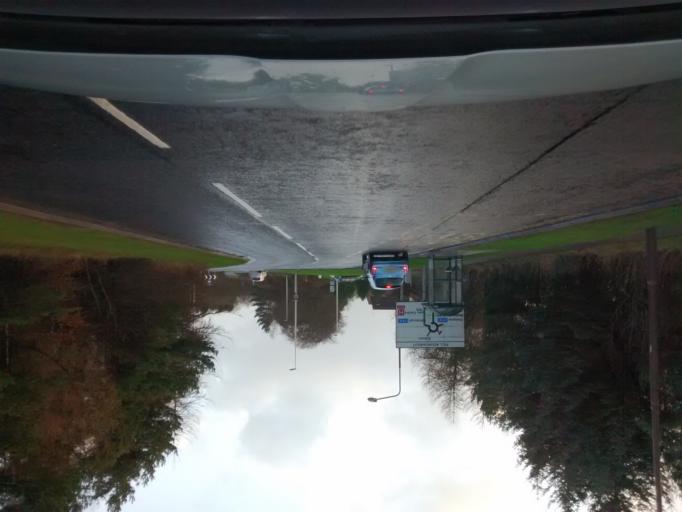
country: GB
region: Scotland
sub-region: West Lothian
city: Livingston
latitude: 55.8869
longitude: -3.5487
